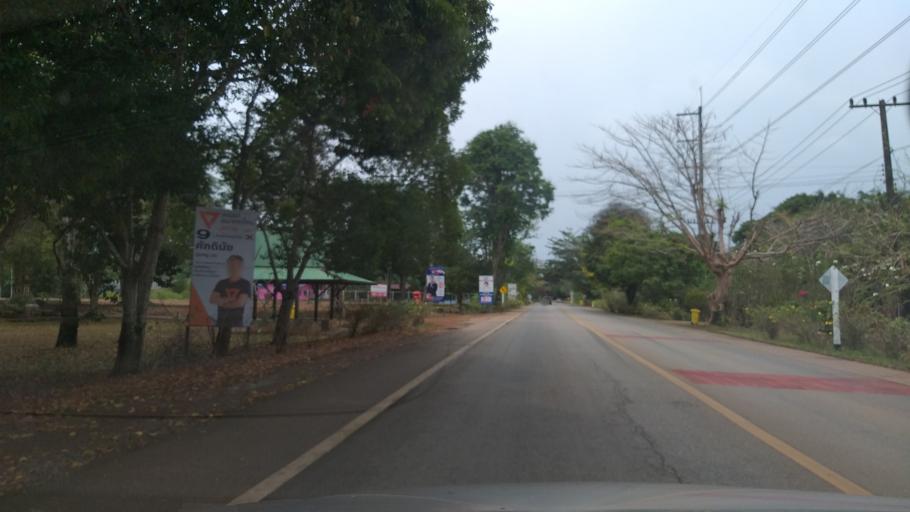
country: TH
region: Trat
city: Laem Ngop
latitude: 12.2292
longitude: 102.3055
